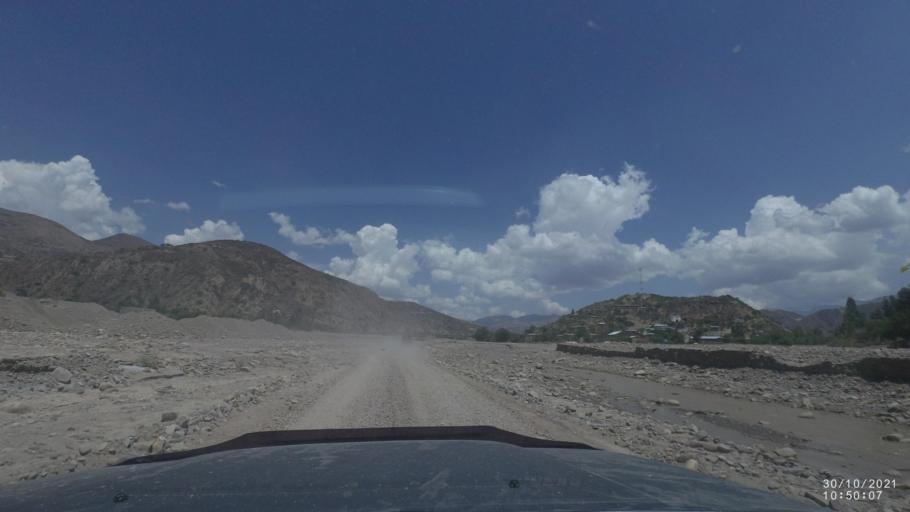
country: BO
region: Cochabamba
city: Sipe Sipe
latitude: -17.5557
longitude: -66.4705
